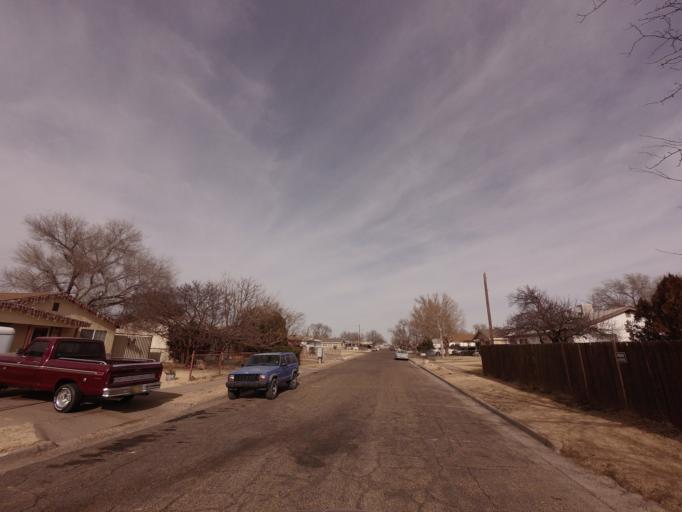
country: US
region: New Mexico
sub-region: Curry County
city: Clovis
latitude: 34.4091
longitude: -103.2385
